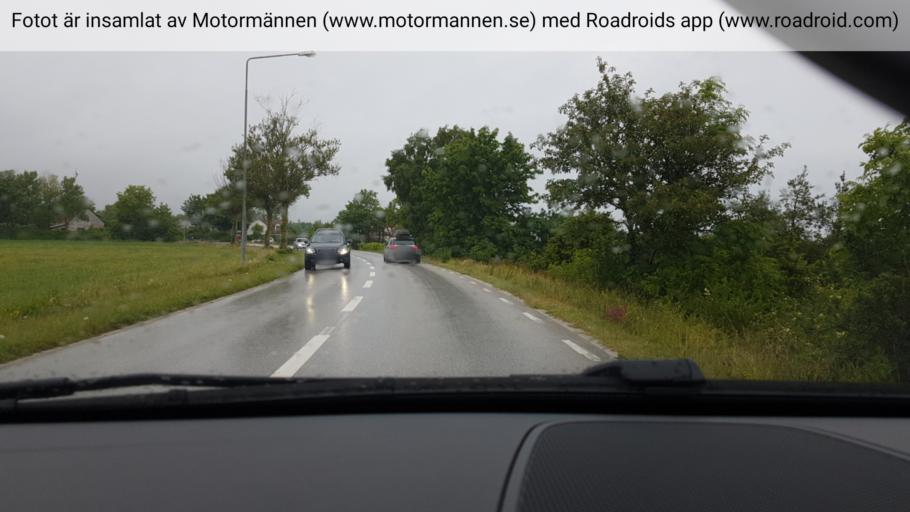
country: SE
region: Gotland
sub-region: Gotland
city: Slite
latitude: 57.8506
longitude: 18.7844
